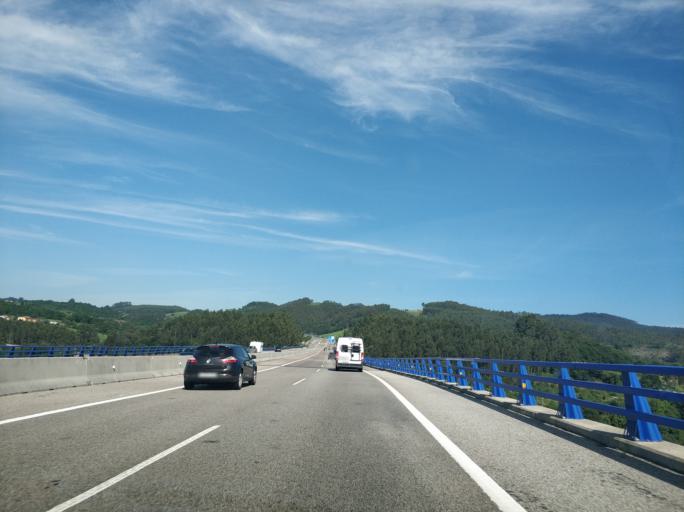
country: ES
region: Asturias
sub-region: Province of Asturias
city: Soto del Barco
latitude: 43.5191
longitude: -6.0800
